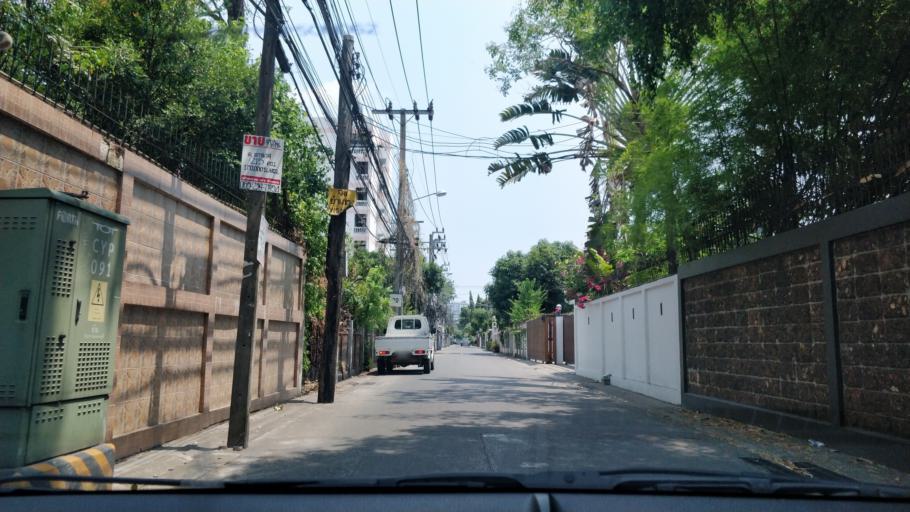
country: TH
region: Bangkok
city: Watthana
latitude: 13.7259
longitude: 100.6033
